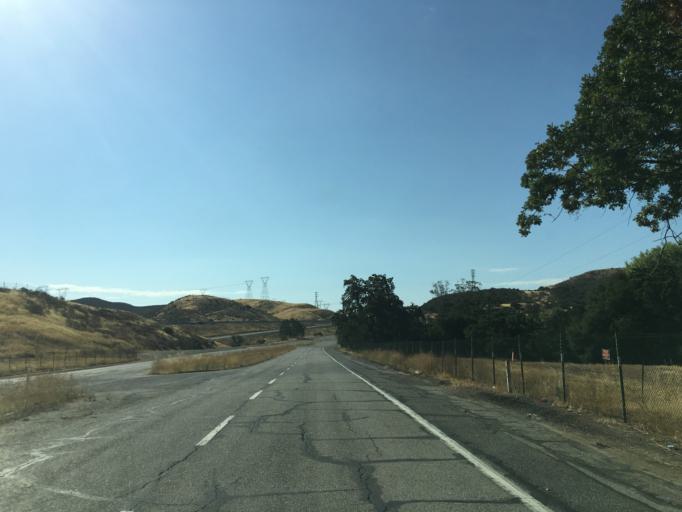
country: US
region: California
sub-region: Los Angeles County
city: Castaic
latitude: 34.5701
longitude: -118.6911
